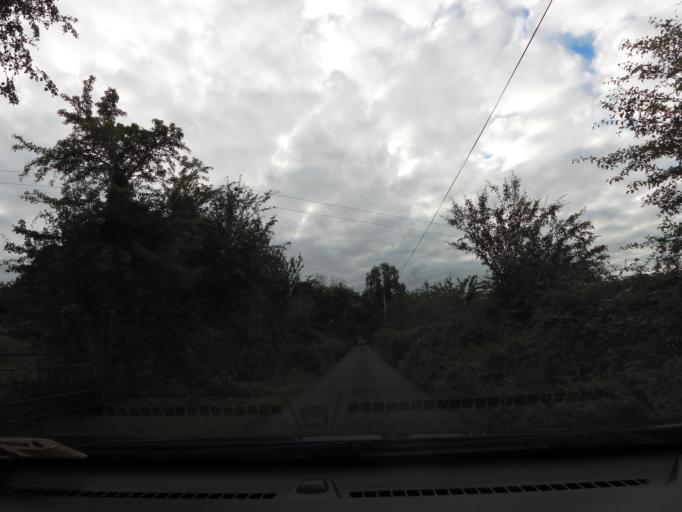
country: IE
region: Connaught
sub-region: County Galway
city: Loughrea
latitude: 53.1356
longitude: -8.4682
